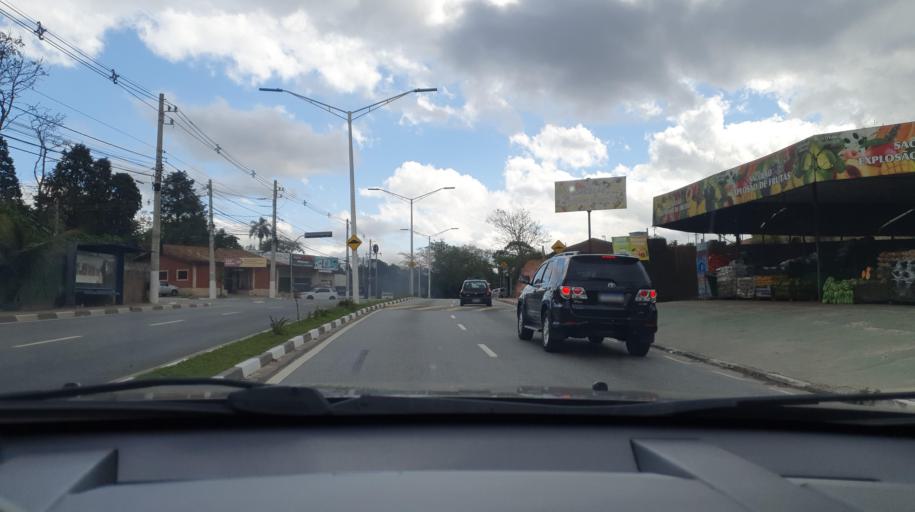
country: BR
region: Sao Paulo
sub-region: Vargem Grande Paulista
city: Vargem Grande Paulista
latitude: -23.6193
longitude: -46.9743
